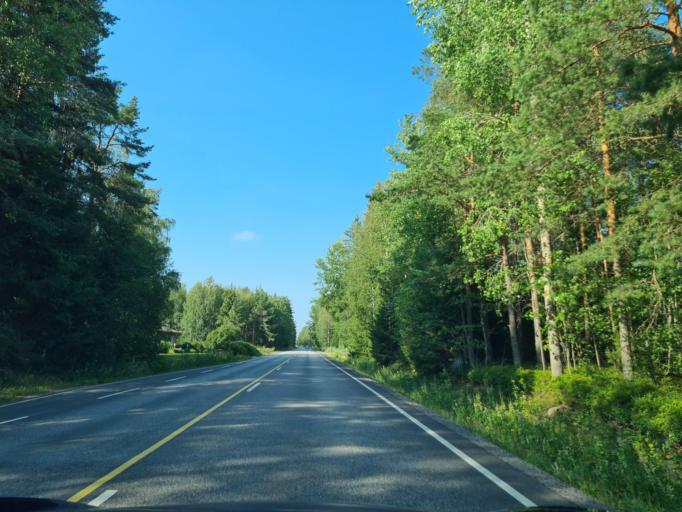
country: FI
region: Satakunta
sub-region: Pohjois-Satakunta
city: Kankaanpaeae
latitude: 61.9437
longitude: 22.5121
